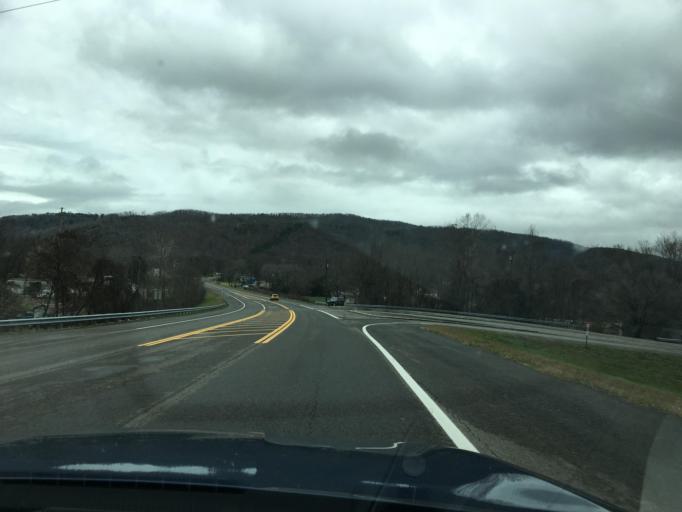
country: US
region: Tennessee
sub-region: Rhea County
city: Spring City
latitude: 35.6960
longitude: -84.8699
